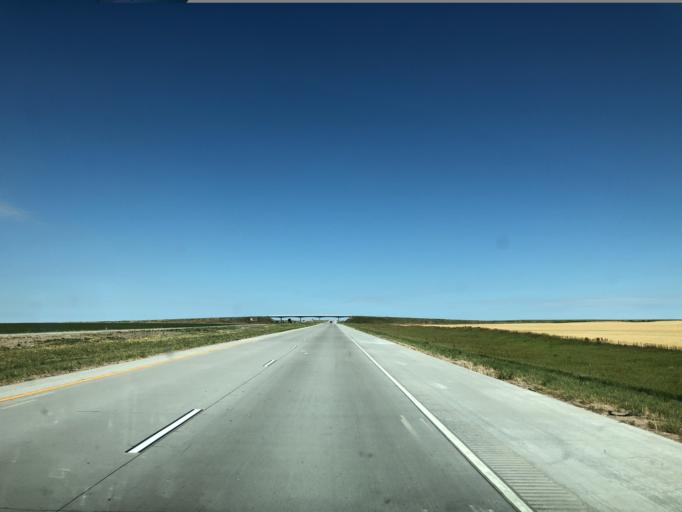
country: US
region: Colorado
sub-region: Kit Carson County
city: Burlington
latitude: 39.2942
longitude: -102.7741
